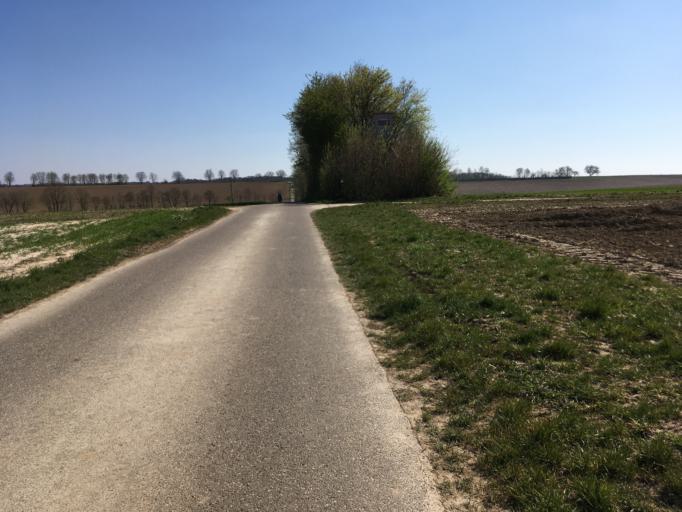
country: DE
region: Baden-Wuerttemberg
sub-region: Regierungsbezirk Stuttgart
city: Massenbachhausen
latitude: 49.1875
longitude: 9.0845
